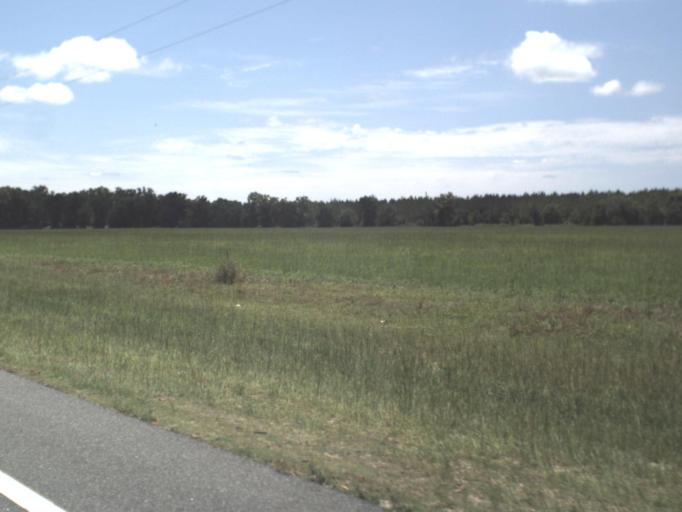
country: US
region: Florida
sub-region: Dixie County
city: Cross City
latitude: 29.8630
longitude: -82.9600
